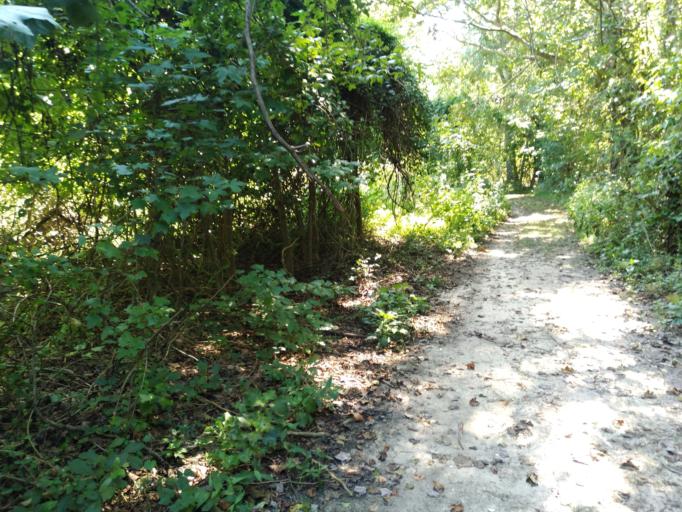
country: US
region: Maryland
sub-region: Calvert County
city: Prince Frederick
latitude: 38.5436
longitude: -76.5385
